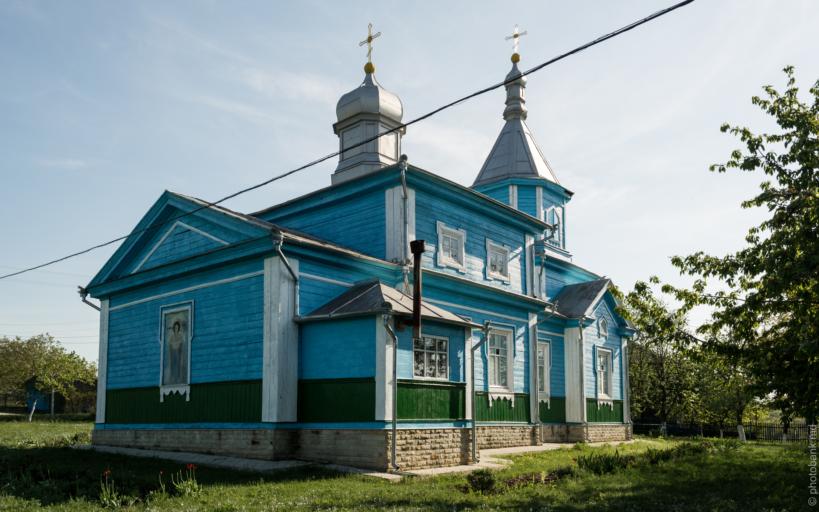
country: MD
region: Balti
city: Balti
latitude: 47.7075
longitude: 27.8697
